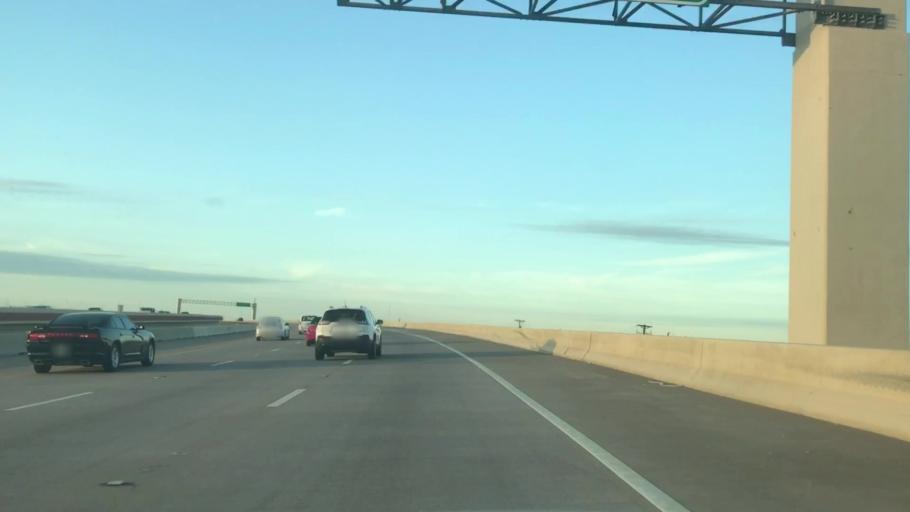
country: US
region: Texas
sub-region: Dallas County
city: Carrollton
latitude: 32.9505
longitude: -96.9255
